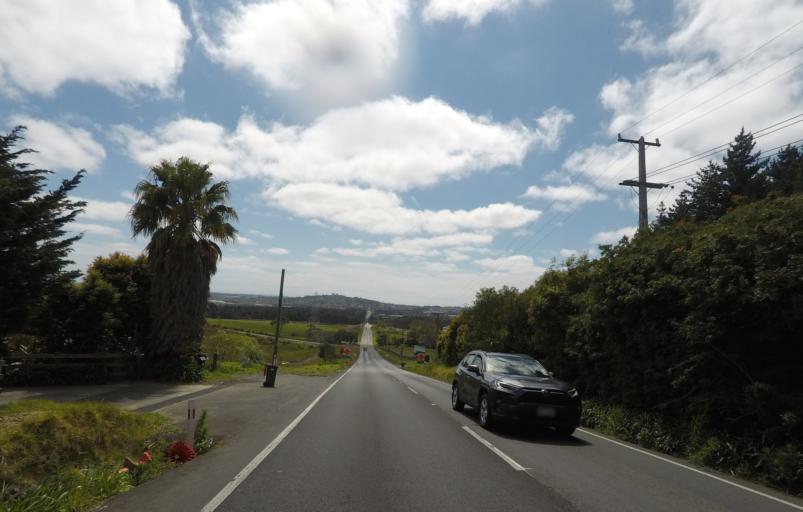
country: NZ
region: Auckland
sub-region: Auckland
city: Manukau City
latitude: -36.9888
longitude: 174.9185
